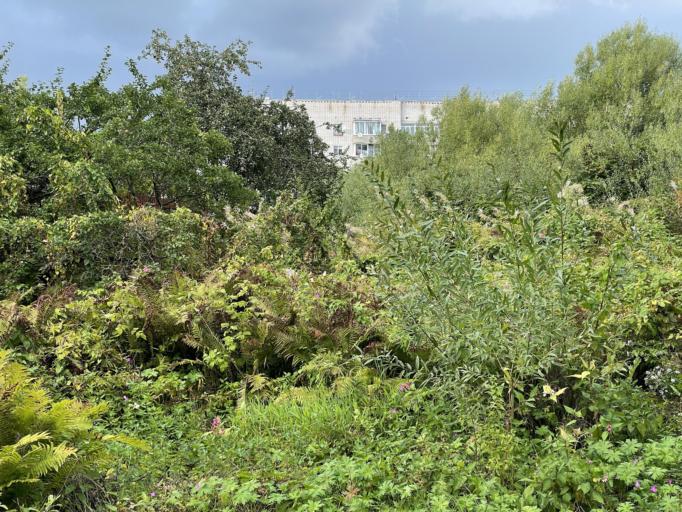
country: RU
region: Tverskaya
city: Vyshniy Volochek
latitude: 57.5877
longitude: 34.5486
